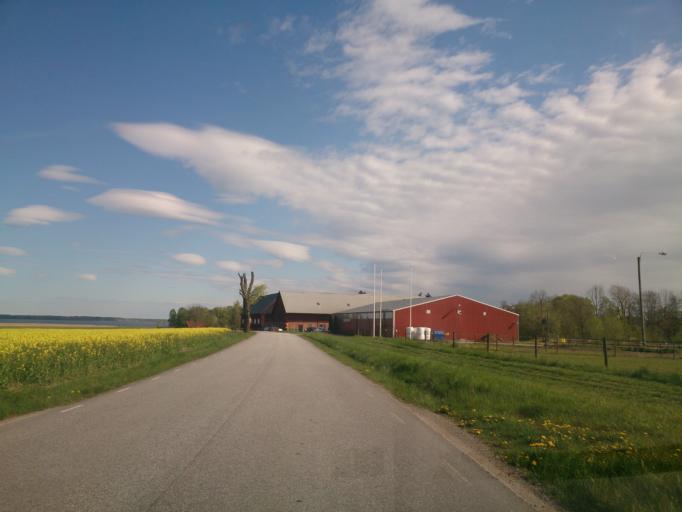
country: SE
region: OEstergoetland
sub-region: Linkopings Kommun
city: Berg
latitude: 58.5034
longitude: 15.5338
